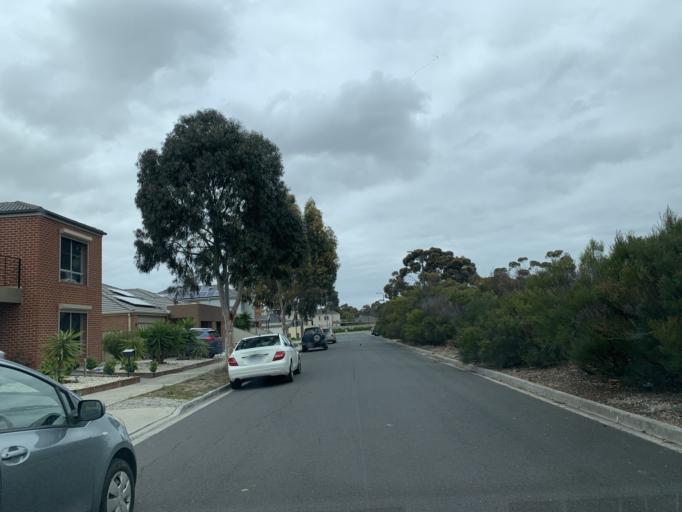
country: AU
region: Victoria
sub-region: Brimbank
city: Cairnlea
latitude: -37.7541
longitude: 144.7920
